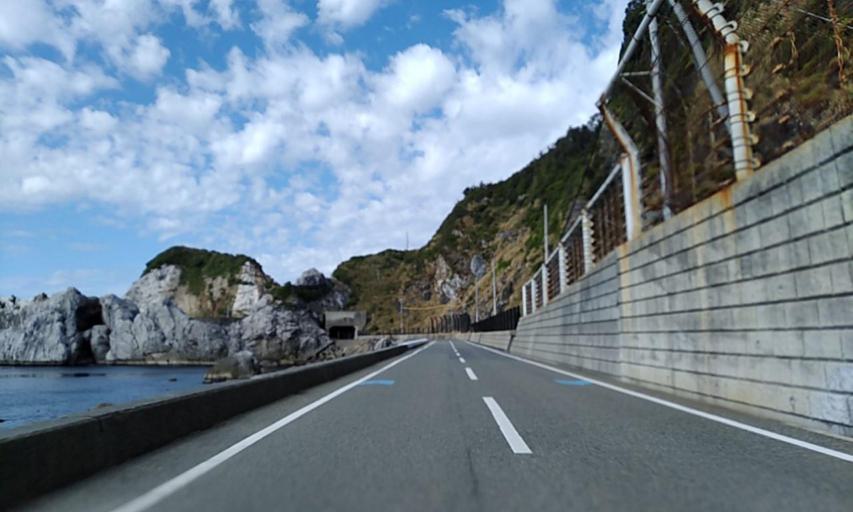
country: JP
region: Wakayama
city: Gobo
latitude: 33.9760
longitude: 135.0754
